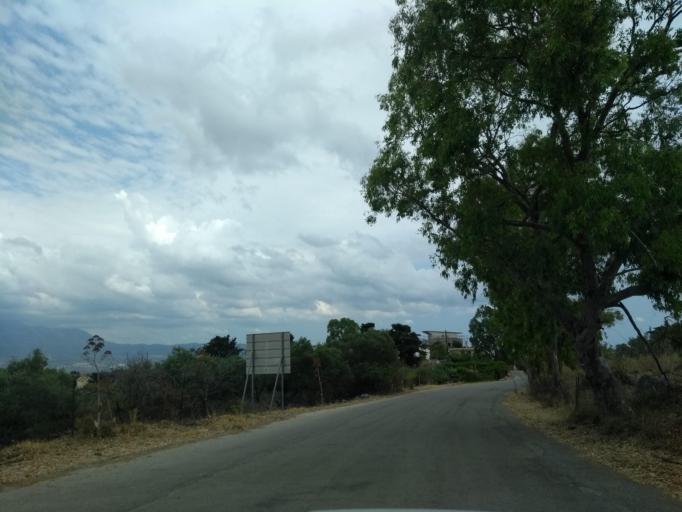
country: GR
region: Crete
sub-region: Nomos Chanias
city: Georgioupolis
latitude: 35.3944
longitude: 24.2360
